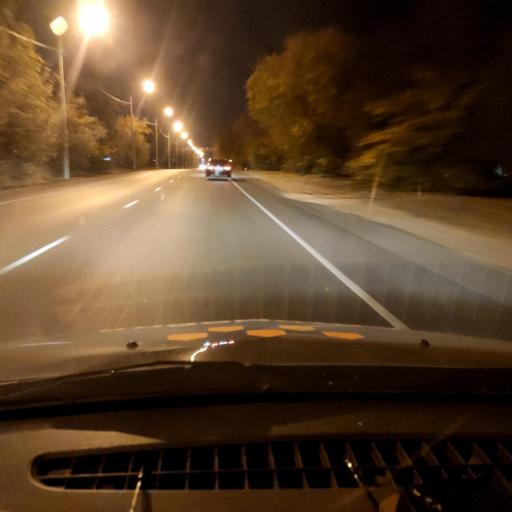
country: RU
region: Voronezj
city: Voronezh
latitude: 51.6104
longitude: 39.1794
